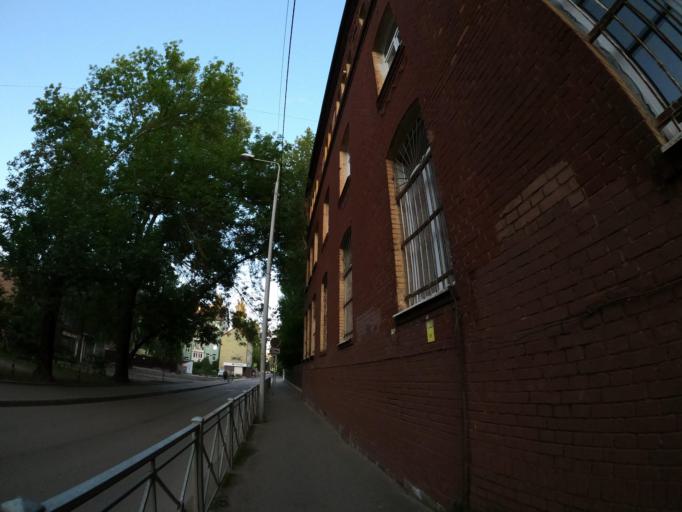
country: RU
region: Kaliningrad
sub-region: Gorod Kaliningrad
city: Kaliningrad
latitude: 54.7122
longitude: 20.5017
